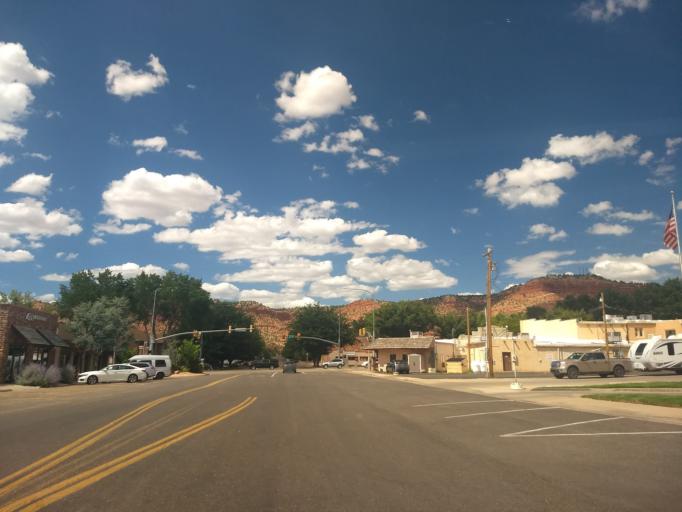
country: US
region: Utah
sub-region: Kane County
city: Kanab
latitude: 37.0473
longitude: -112.5285
